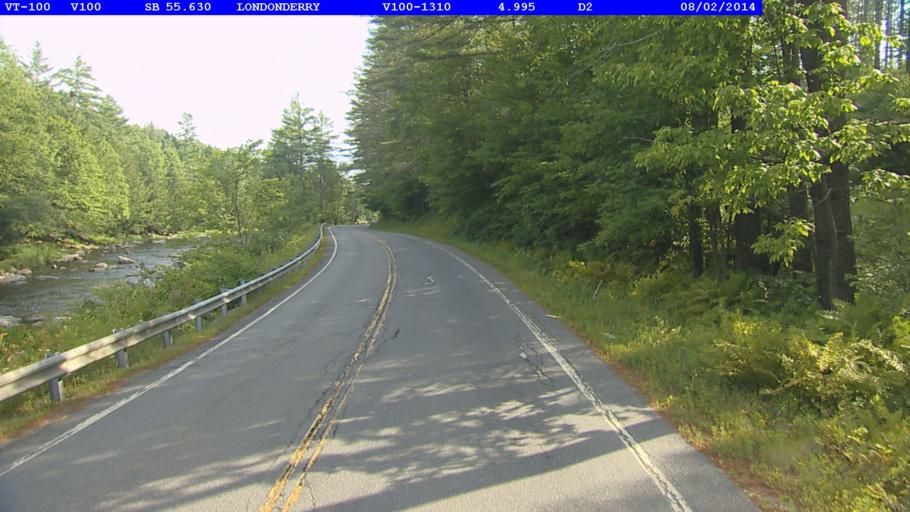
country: US
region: Vermont
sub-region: Windsor County
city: Chester
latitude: 43.2190
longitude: -72.8221
